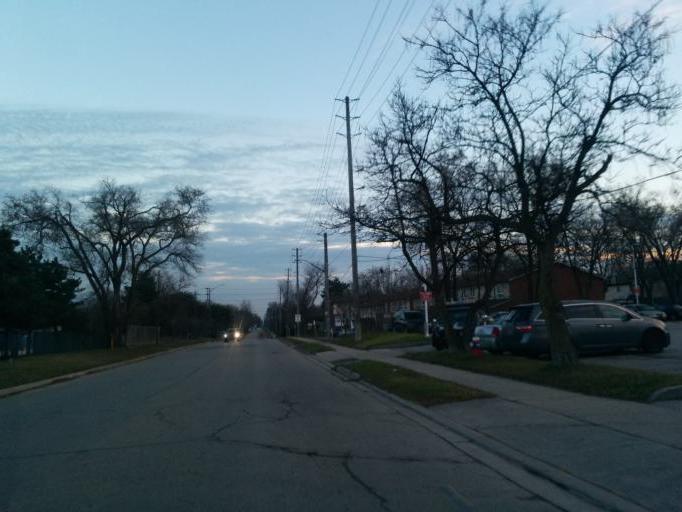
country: CA
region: Ontario
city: Etobicoke
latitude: 43.5923
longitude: -79.5729
